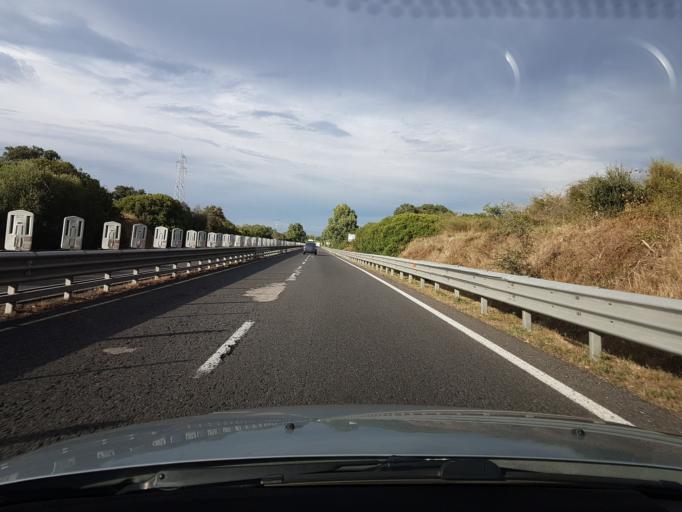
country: IT
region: Sardinia
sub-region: Provincia di Oristano
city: Paulilatino
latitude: 40.1024
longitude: 8.7860
